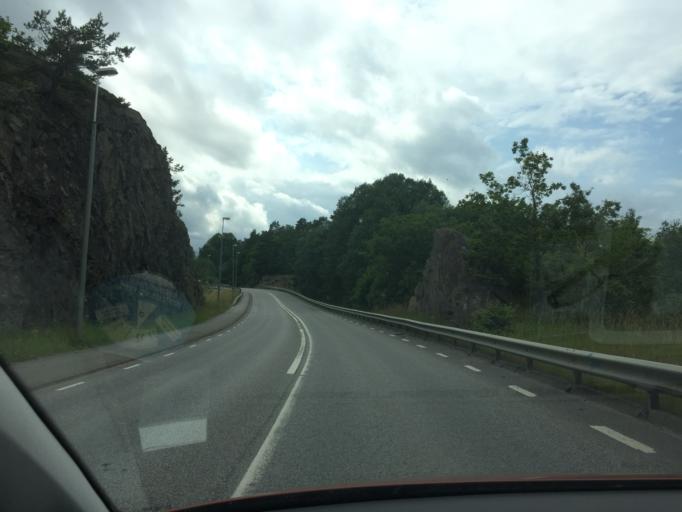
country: SE
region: Stockholm
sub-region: Botkyrka Kommun
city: Tullinge
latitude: 59.2008
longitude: 17.8744
